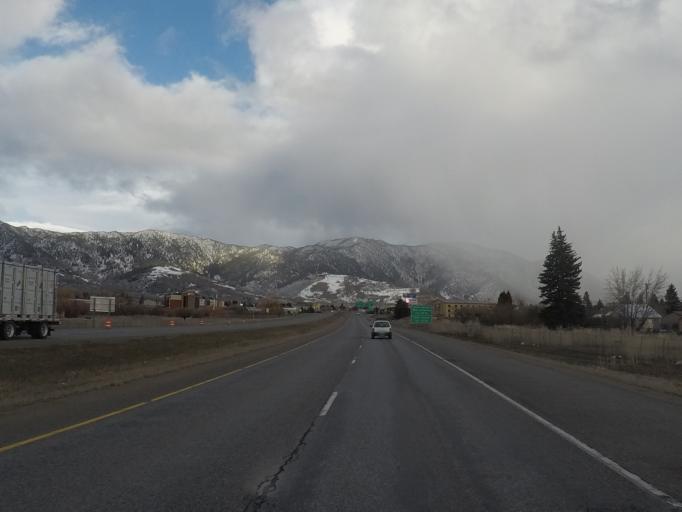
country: US
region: Montana
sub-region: Silver Bow County
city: Butte
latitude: 45.9863
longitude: -112.5161
